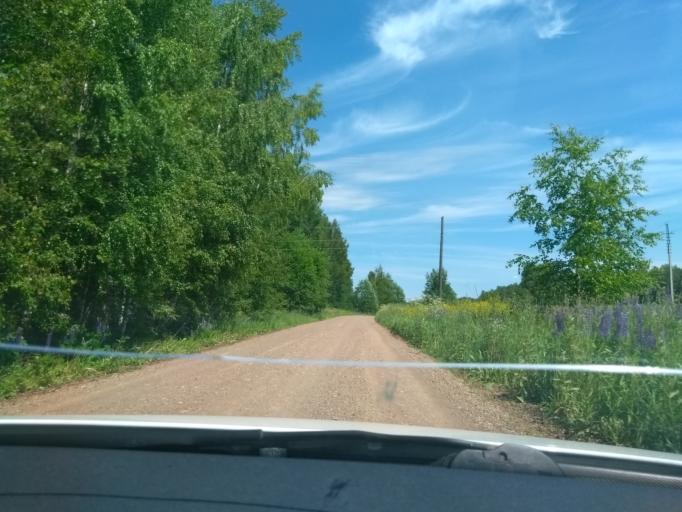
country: RU
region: Perm
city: Sylva
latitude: 57.8168
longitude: 56.7298
